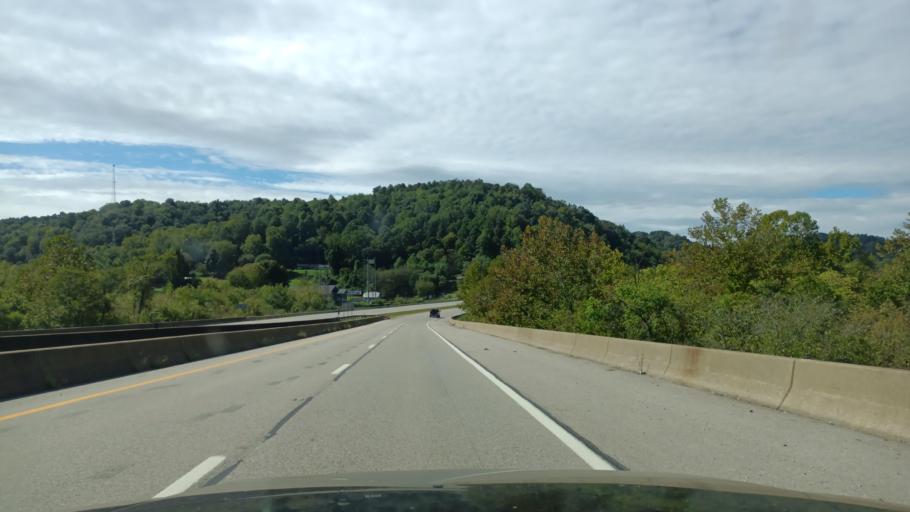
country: US
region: West Virginia
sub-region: Doddridge County
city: West Union
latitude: 39.2866
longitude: -80.7289
